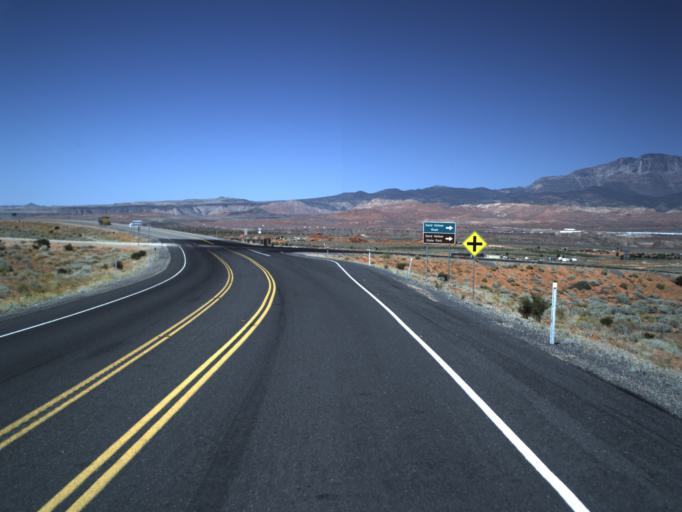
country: US
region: Utah
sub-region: Washington County
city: Washington
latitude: 37.1060
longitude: -113.3955
